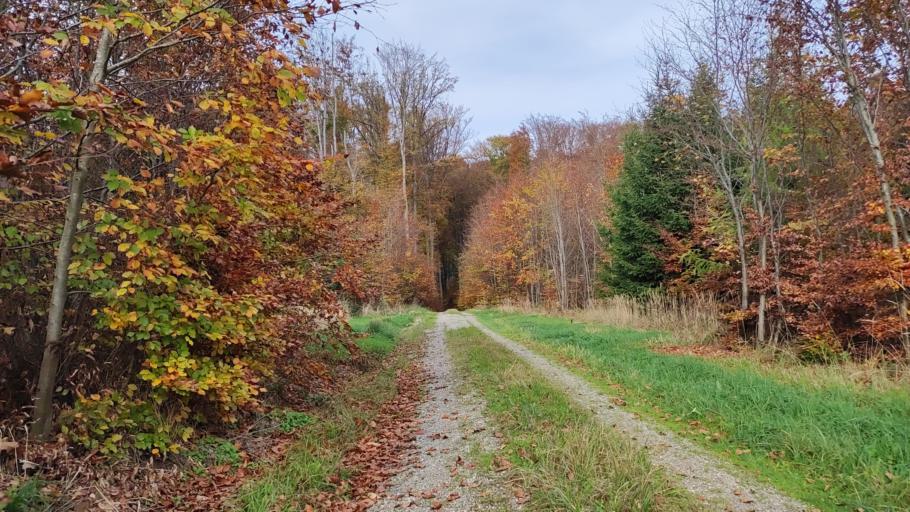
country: DE
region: Bavaria
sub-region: Swabia
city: Langenneufnach
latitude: 48.2705
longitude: 10.5697
